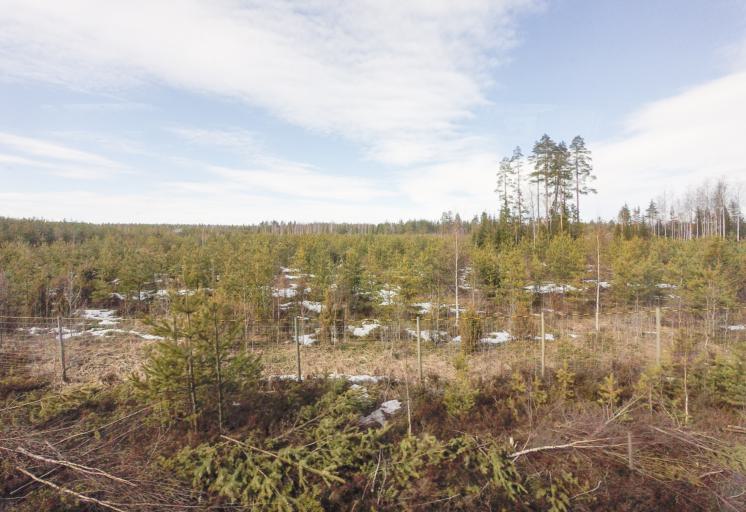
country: FI
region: South Karelia
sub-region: Lappeenranta
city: Joutseno
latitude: 61.1090
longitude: 28.4432
